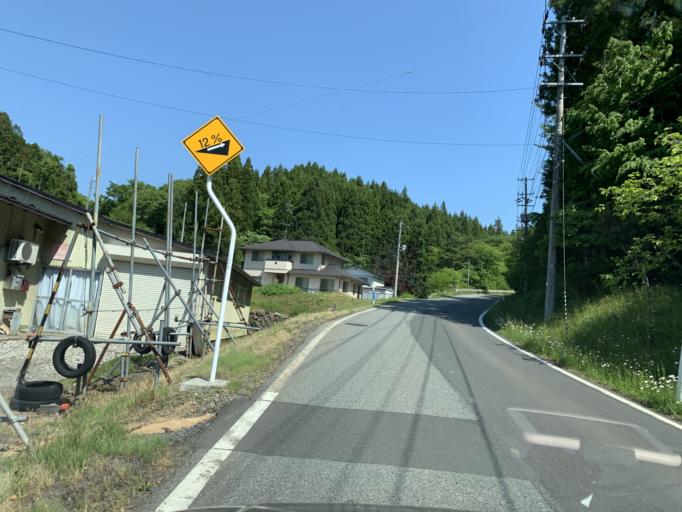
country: JP
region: Iwate
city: Mizusawa
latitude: 39.0459
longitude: 141.0661
